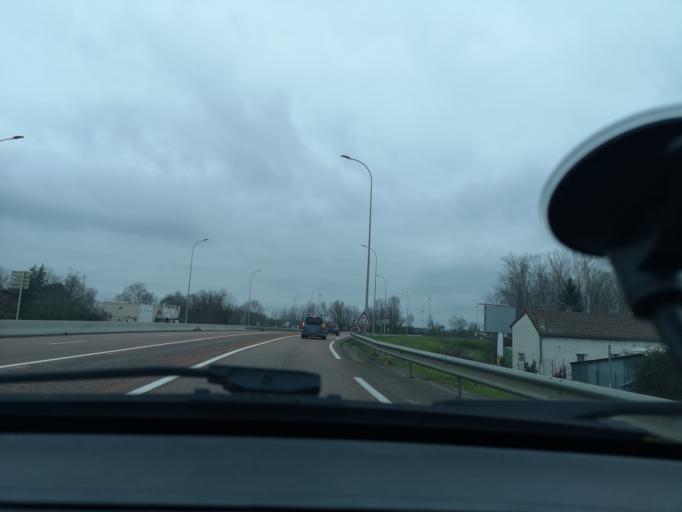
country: FR
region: Bourgogne
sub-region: Departement de Saone-et-Loire
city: Champforgeuil
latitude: 46.7998
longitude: 4.8337
